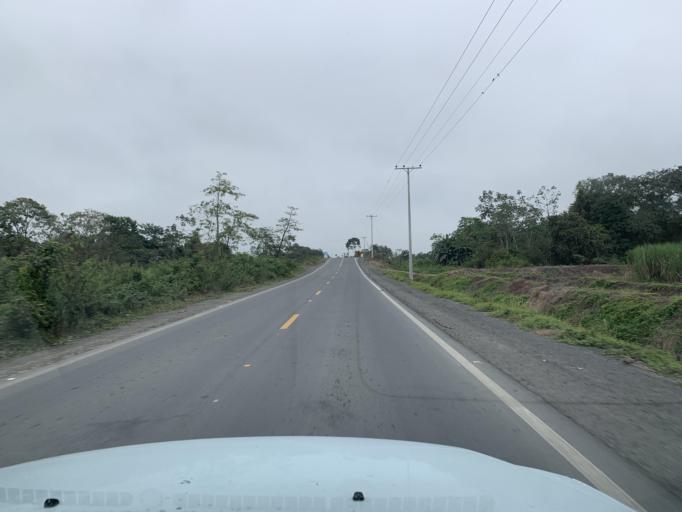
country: EC
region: Guayas
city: Coronel Marcelino Mariduena
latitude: -2.3339
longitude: -79.5282
